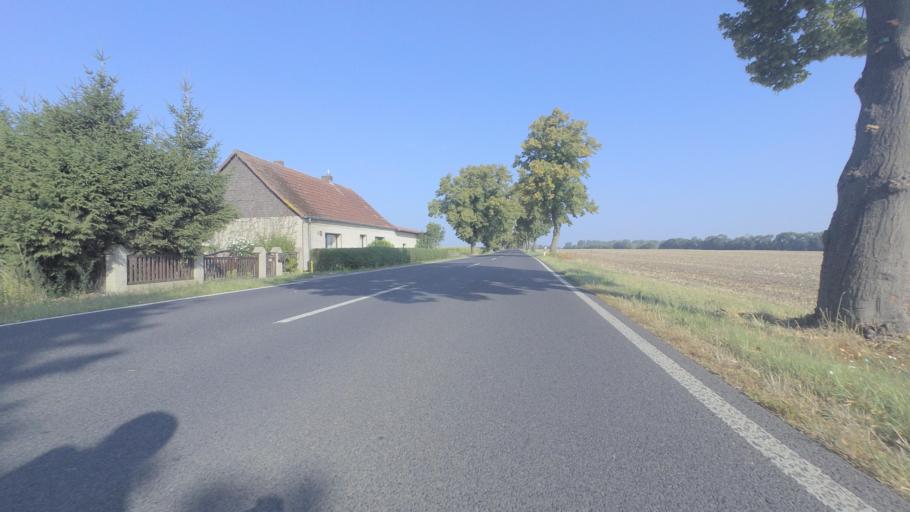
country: DE
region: Brandenburg
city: Fehrbellin
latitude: 52.7800
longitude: 12.8295
